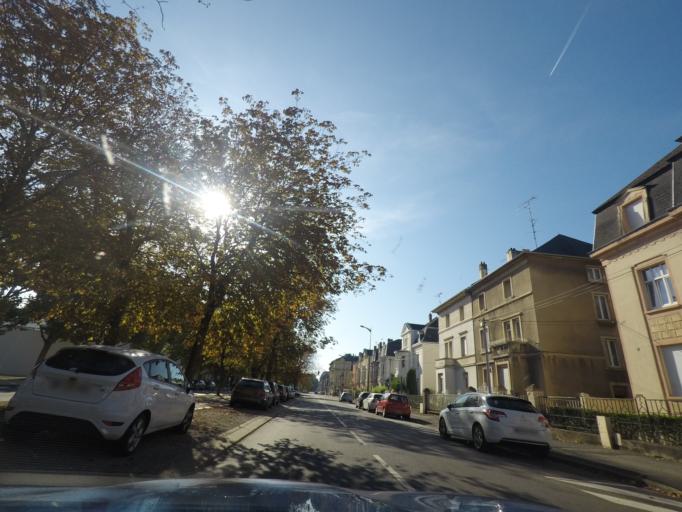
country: FR
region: Lorraine
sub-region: Departement de la Moselle
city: Thionville
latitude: 49.3593
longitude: 6.1598
